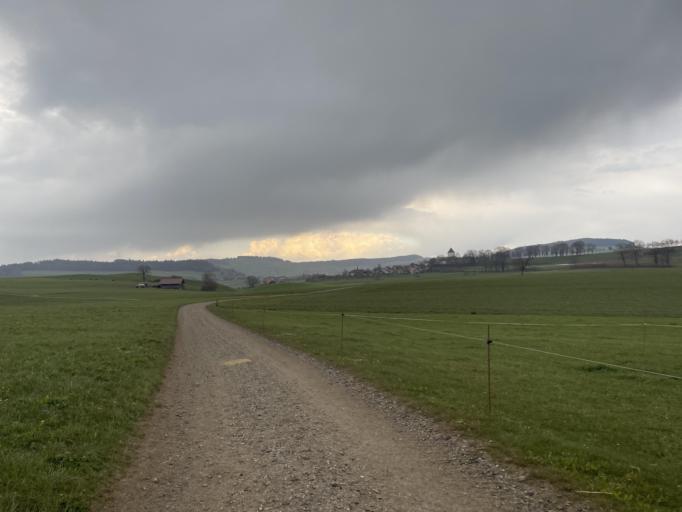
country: CH
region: Bern
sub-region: Bern-Mittelland District
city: Taegertschi
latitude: 46.9024
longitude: 7.5950
